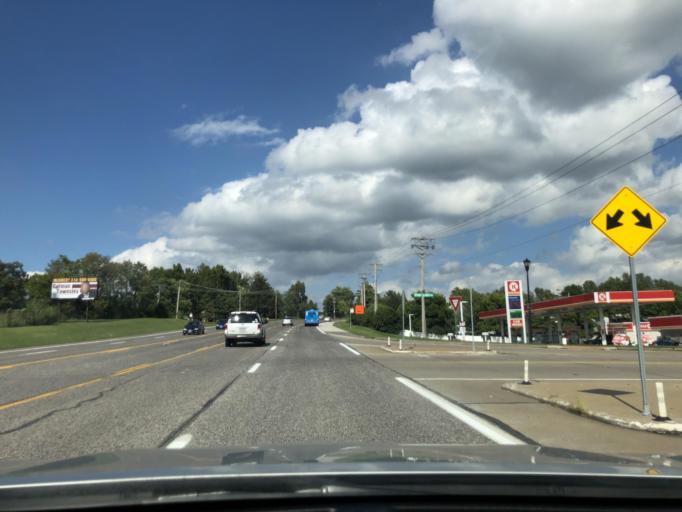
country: US
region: Missouri
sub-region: Saint Louis County
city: Lakeshire
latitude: 38.5349
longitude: -90.3387
